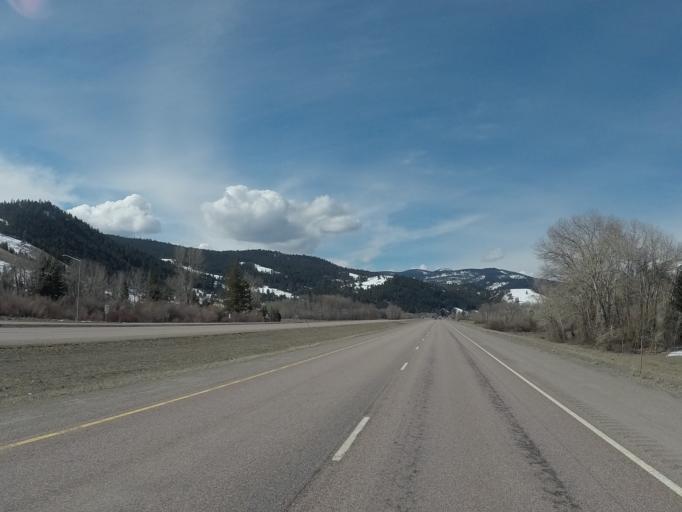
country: US
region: Montana
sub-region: Granite County
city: Philipsburg
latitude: 46.7039
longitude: -113.3395
